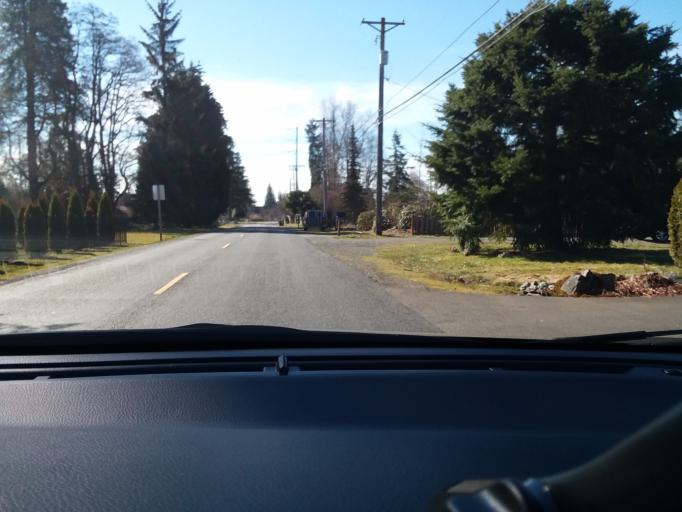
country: US
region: Washington
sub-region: Pierce County
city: Midland
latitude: 47.1712
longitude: -122.3972
